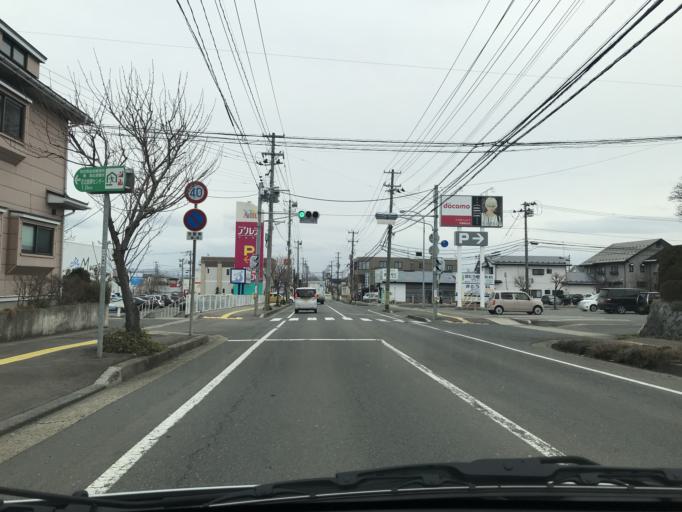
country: JP
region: Iwate
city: Hanamaki
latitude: 39.3985
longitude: 141.1062
